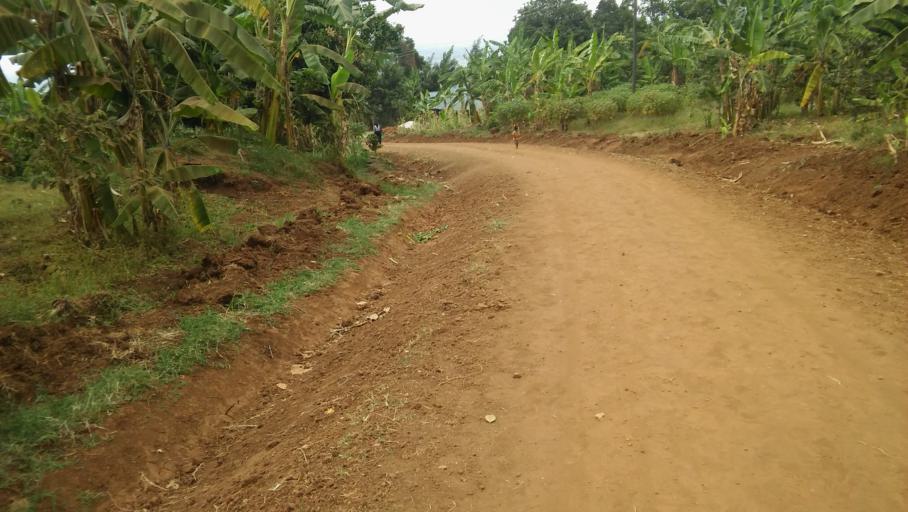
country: UG
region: Eastern Region
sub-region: Mbale District
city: Mbale
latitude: 1.0575
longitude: 34.2176
